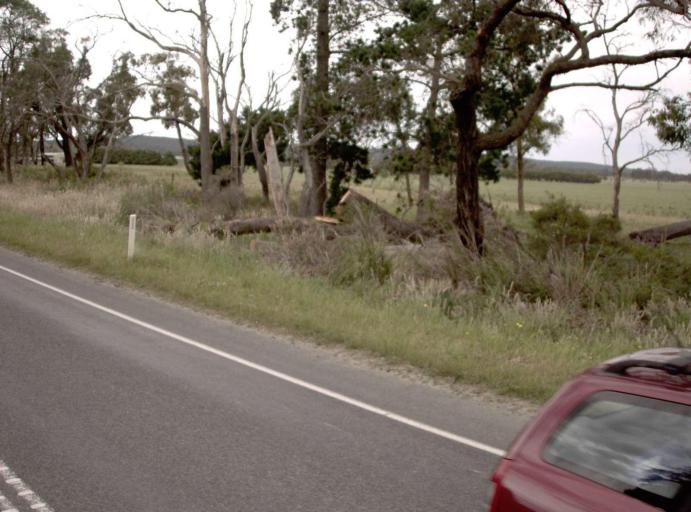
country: AU
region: Victoria
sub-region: Cardinia
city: Koo-Wee-Rup
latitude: -38.3220
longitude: 145.5861
